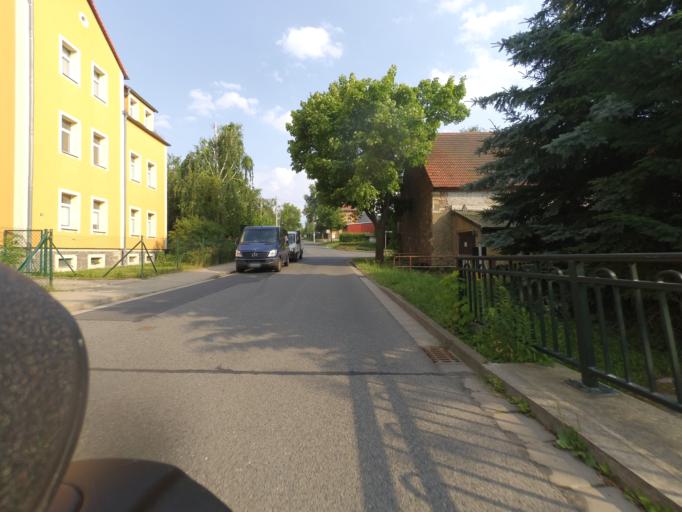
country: DE
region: Saxony
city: Wilsdruff
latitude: 51.0488
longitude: 13.5401
